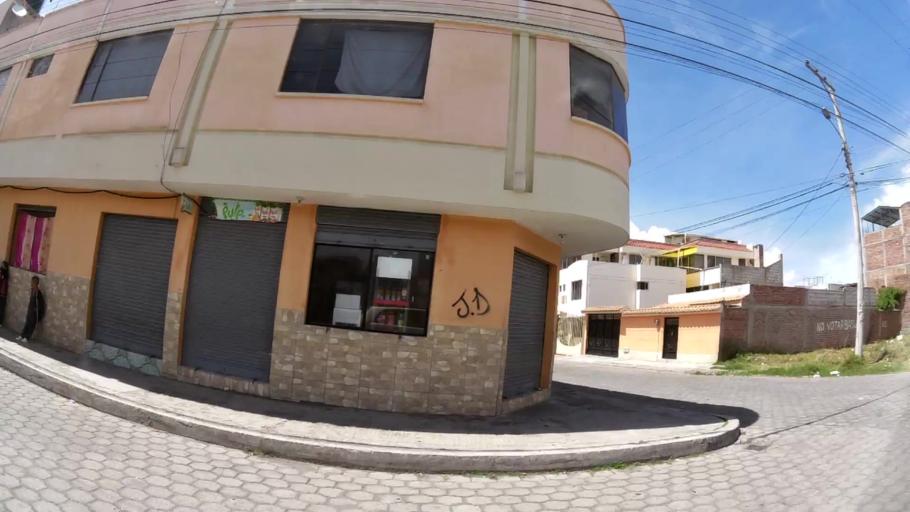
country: EC
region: Chimborazo
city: Riobamba
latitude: -1.6599
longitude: -78.6398
